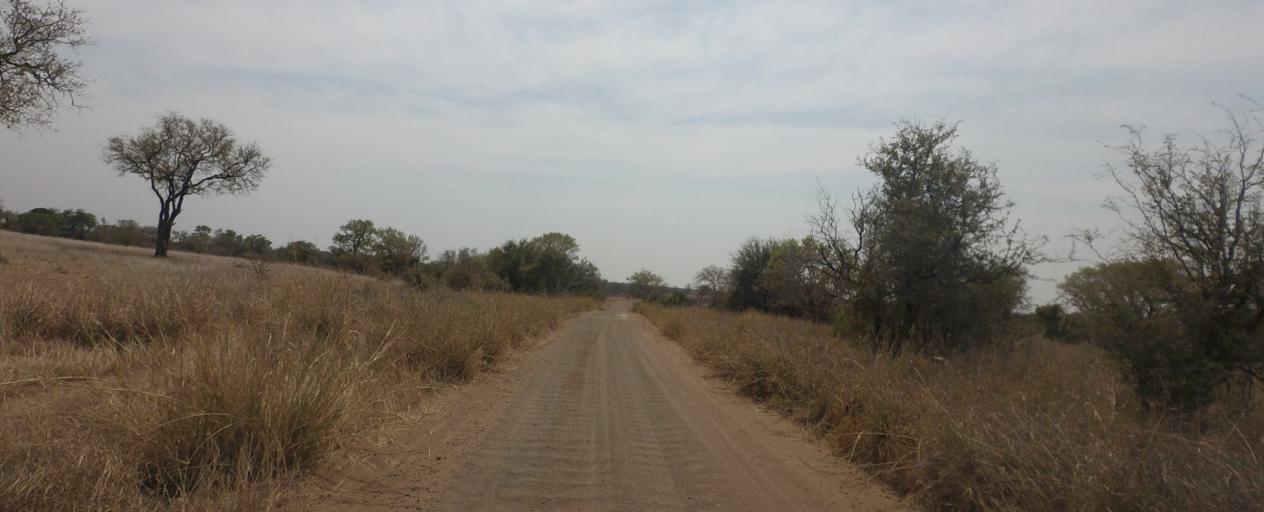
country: ZA
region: Limpopo
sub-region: Mopani District Municipality
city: Phalaborwa
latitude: -24.2608
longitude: 31.6506
